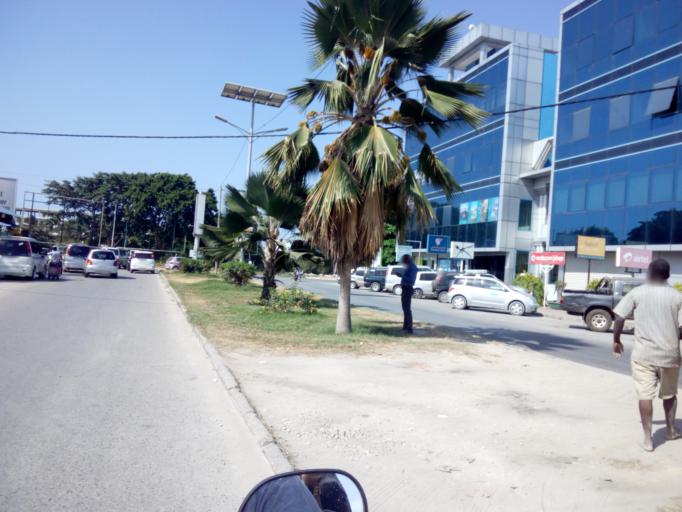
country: TZ
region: Zanzibar Urban/West
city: Zanzibar
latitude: -6.1596
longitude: 39.1990
